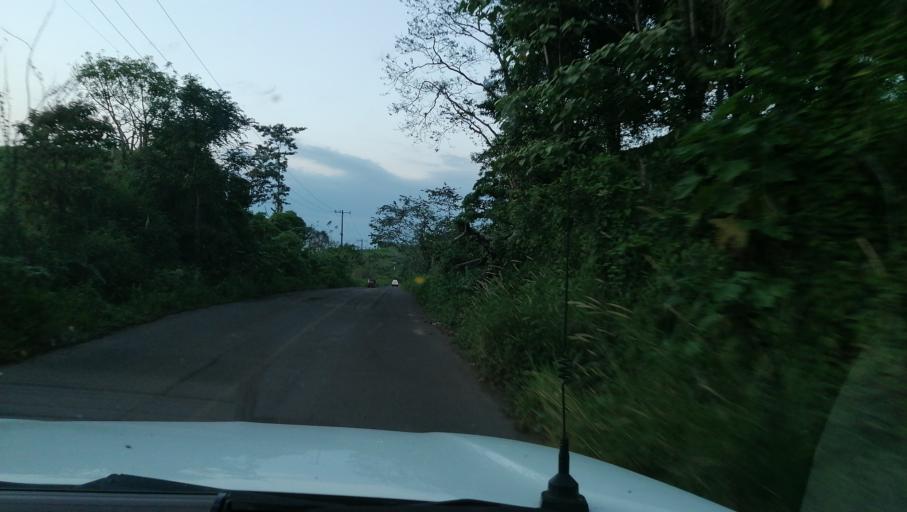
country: MX
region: Chiapas
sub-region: Ostuacan
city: Nuevo Juan del Grijalva
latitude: 17.4344
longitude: -93.3509
